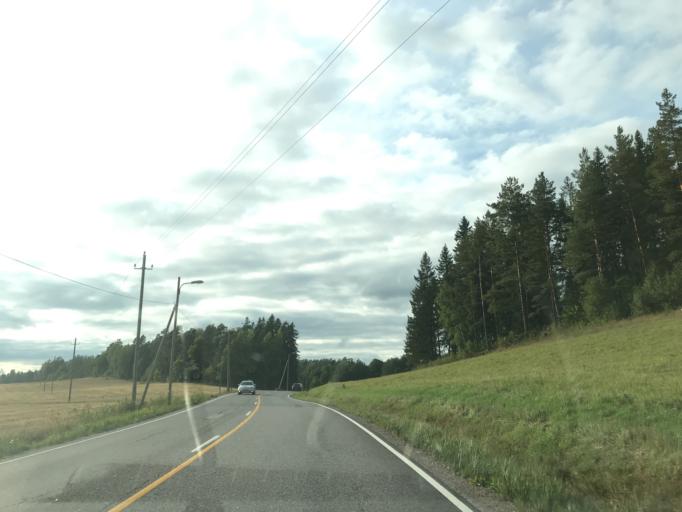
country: FI
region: Uusimaa
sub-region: Helsinki
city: Kirkkonummi
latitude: 60.2030
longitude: 24.5191
